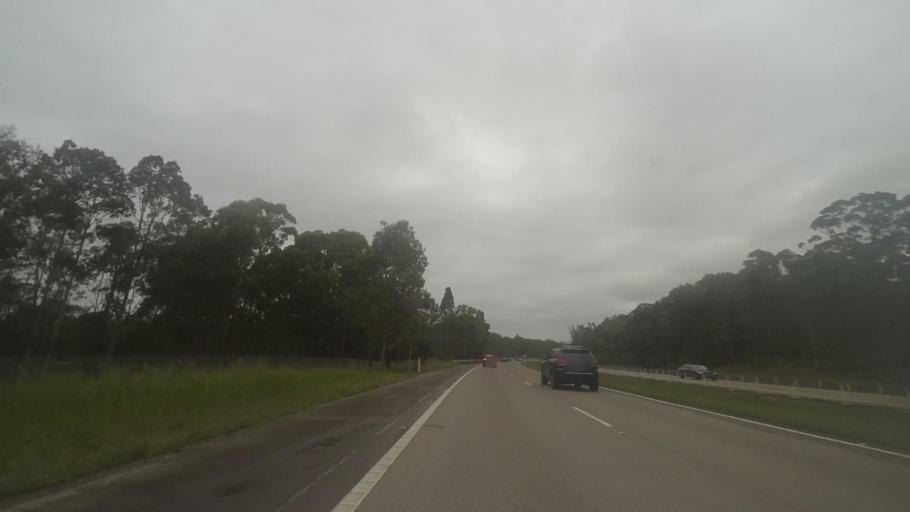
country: AU
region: New South Wales
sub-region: Port Stephens Shire
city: Medowie
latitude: -32.6925
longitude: 151.8088
